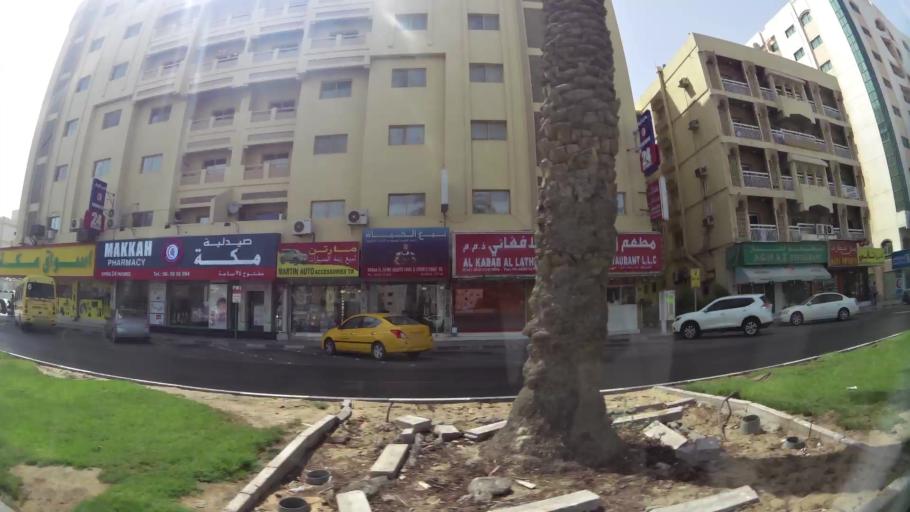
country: AE
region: Ash Shariqah
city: Sharjah
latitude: 25.3682
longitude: 55.4033
